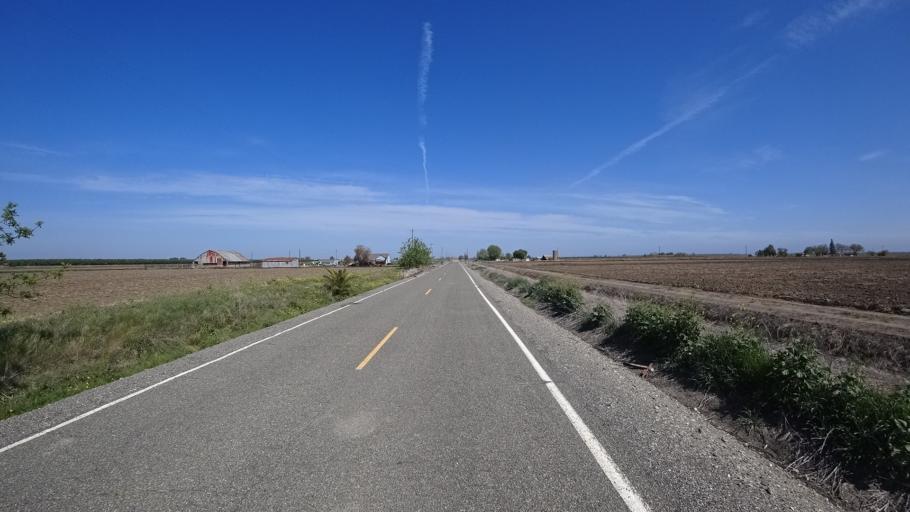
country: US
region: California
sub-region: Glenn County
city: Hamilton City
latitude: 39.6065
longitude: -122.0369
